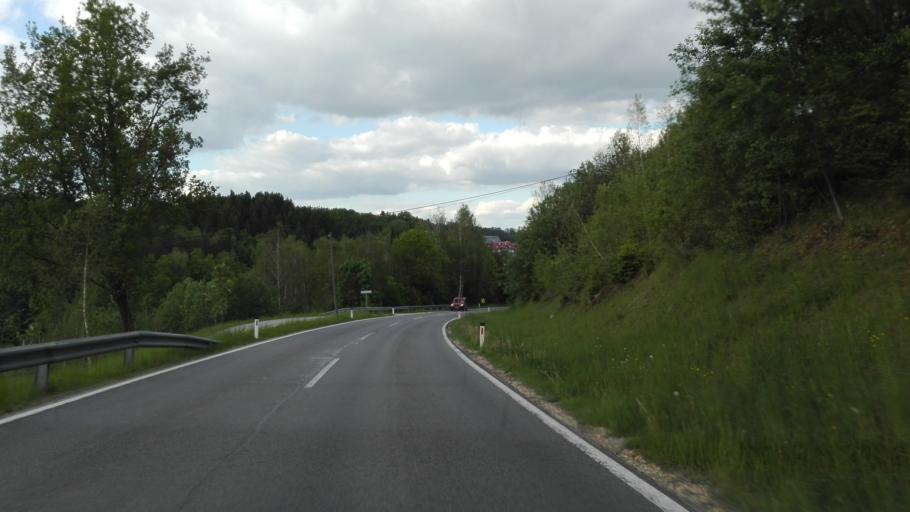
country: AT
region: Upper Austria
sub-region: Politischer Bezirk Perg
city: Bad Kreuzen
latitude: 48.3945
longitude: 14.7207
